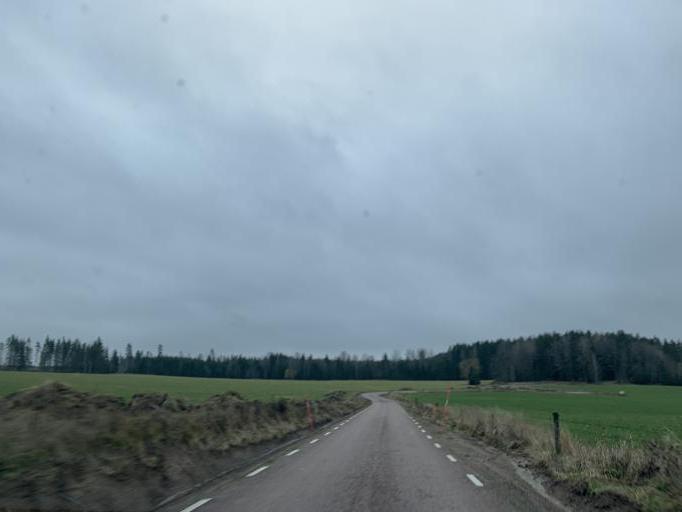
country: SE
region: Vaestmanland
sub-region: Kopings Kommun
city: Koping
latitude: 59.6507
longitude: 16.0734
